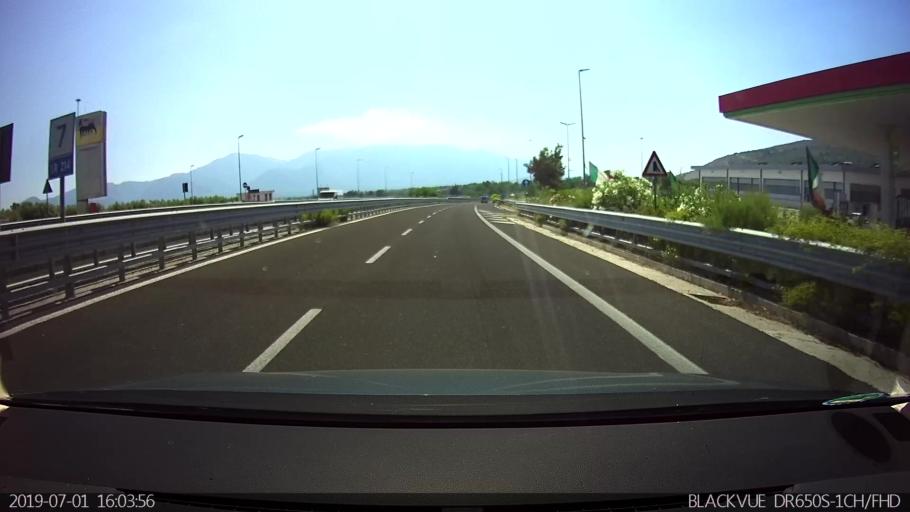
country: IT
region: Latium
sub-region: Provincia di Frosinone
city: Tecchiena
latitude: 41.6697
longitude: 13.3220
